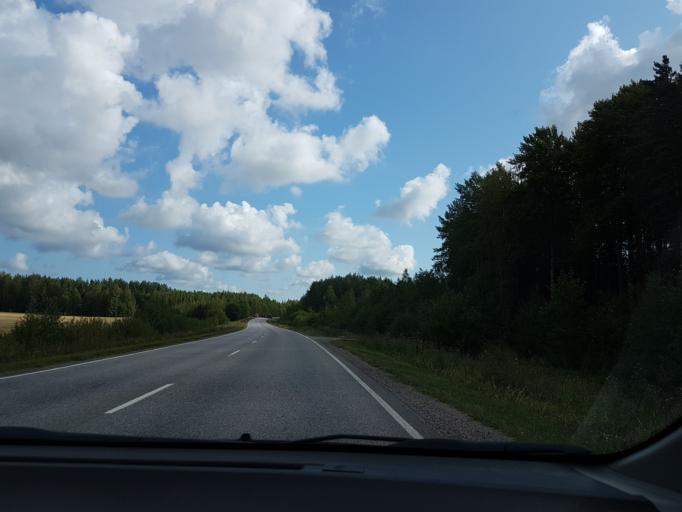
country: FI
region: Uusimaa
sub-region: Helsinki
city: Pornainen
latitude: 60.4687
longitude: 25.2943
